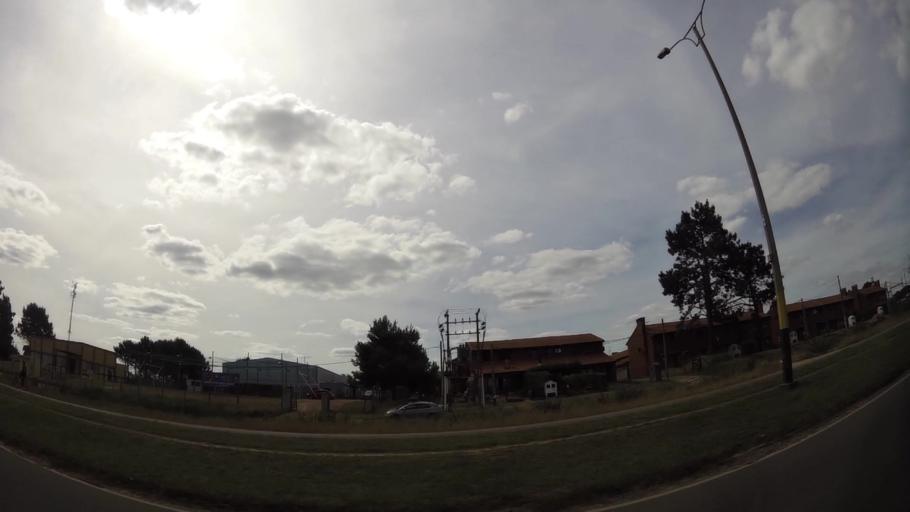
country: UY
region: Canelones
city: Pando
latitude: -34.8127
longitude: -55.9413
